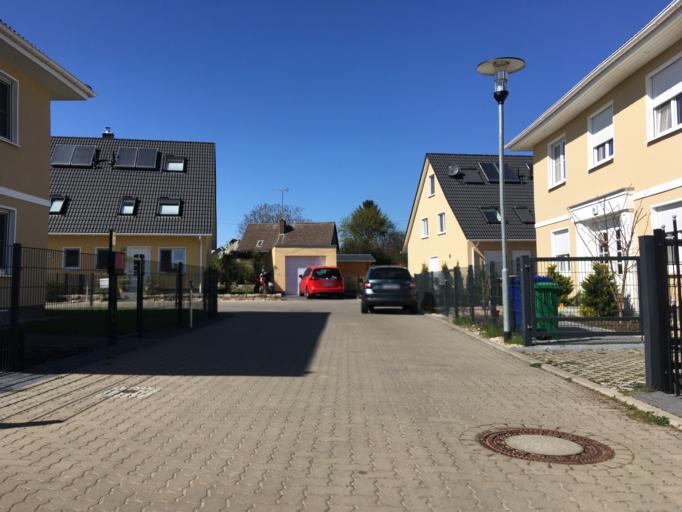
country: DE
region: Berlin
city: Gropiusstadt
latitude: 52.4188
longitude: 13.4545
